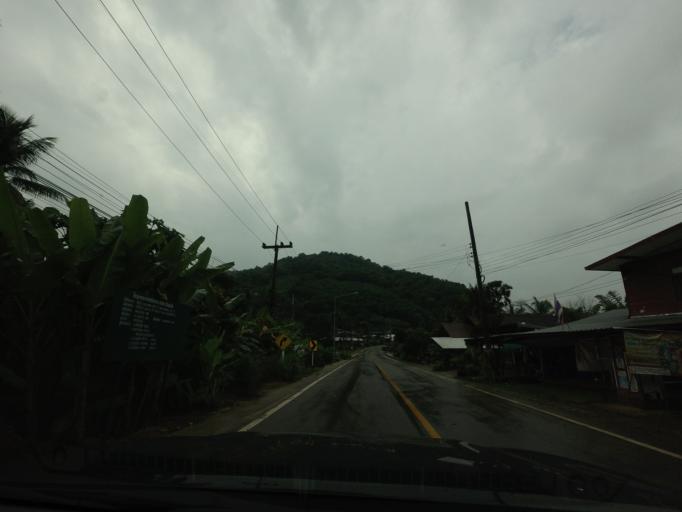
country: TH
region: Nong Khai
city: Sangkhom
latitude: 18.2040
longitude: 102.1189
